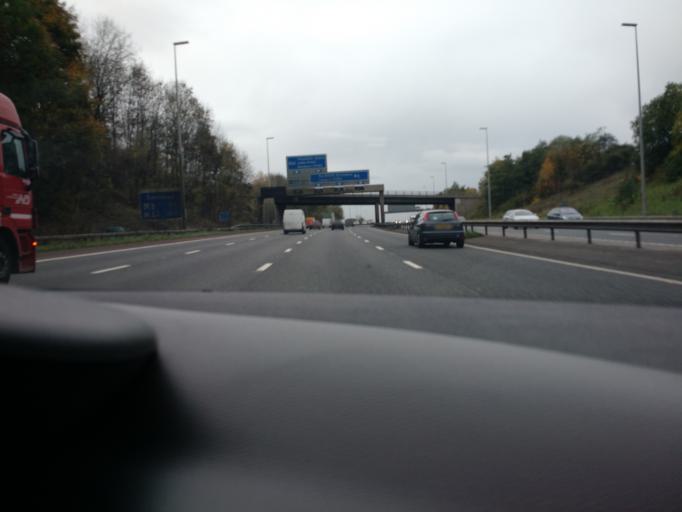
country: GB
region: England
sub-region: Lancashire
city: Clayton-le-Woods
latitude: 53.7558
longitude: -2.6384
